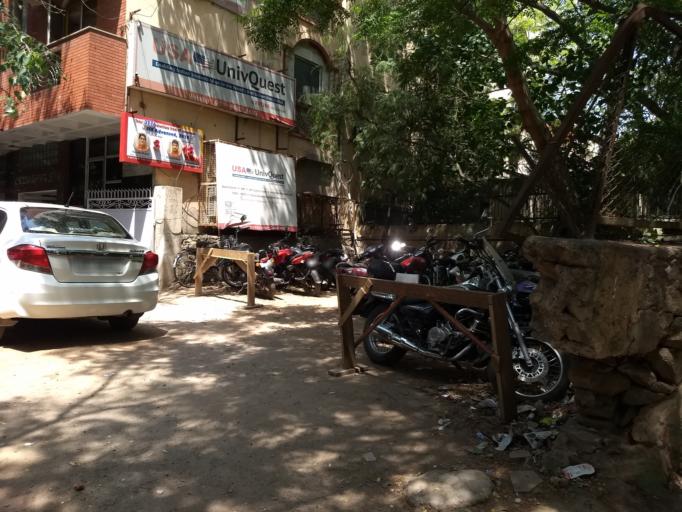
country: IN
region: NCT
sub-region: New Delhi
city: New Delhi
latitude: 28.5413
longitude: 77.2033
